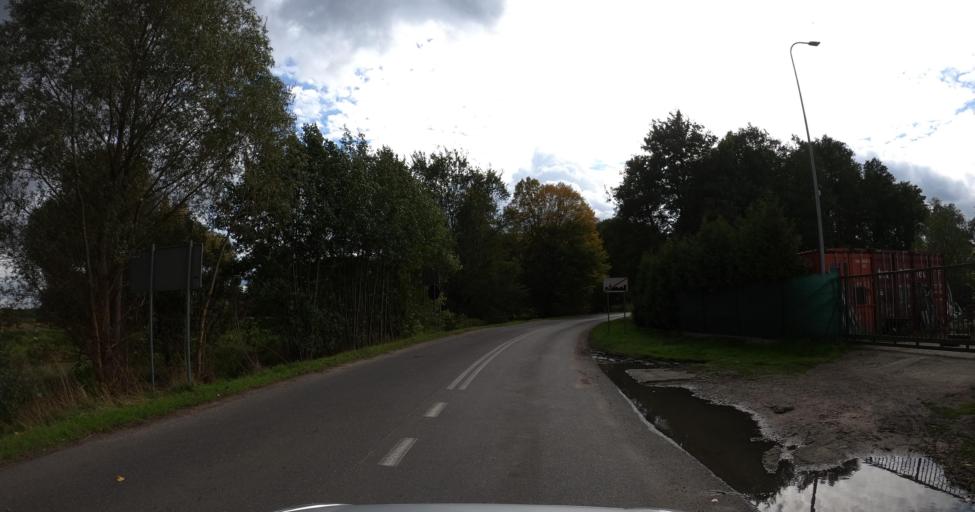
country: PL
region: Lubusz
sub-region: Zielona Gora
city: Zielona Gora
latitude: 51.9943
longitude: 15.5659
